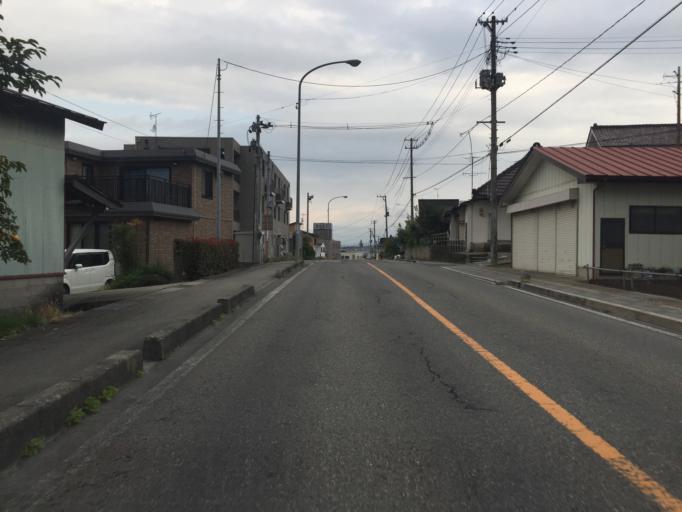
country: JP
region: Fukushima
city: Kitakata
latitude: 37.4941
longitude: 139.9495
